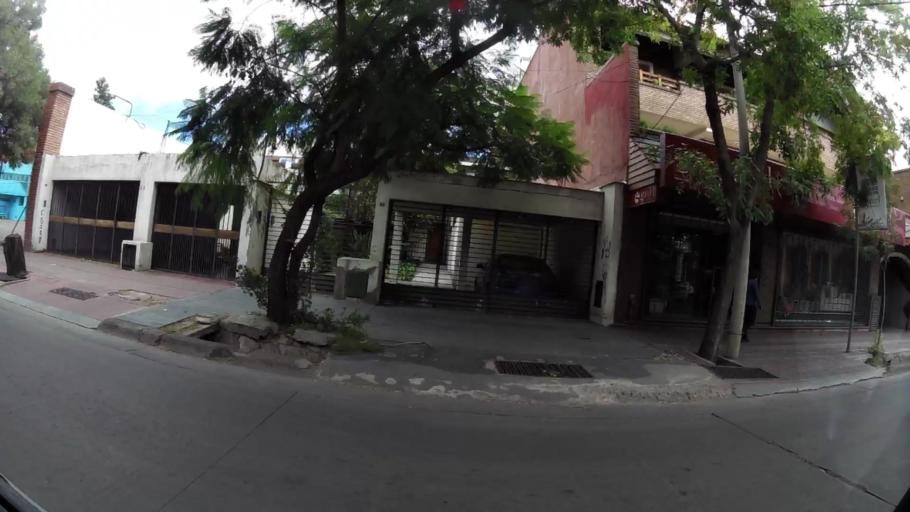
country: AR
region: Mendoza
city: Mendoza
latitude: -32.9007
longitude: -68.8599
